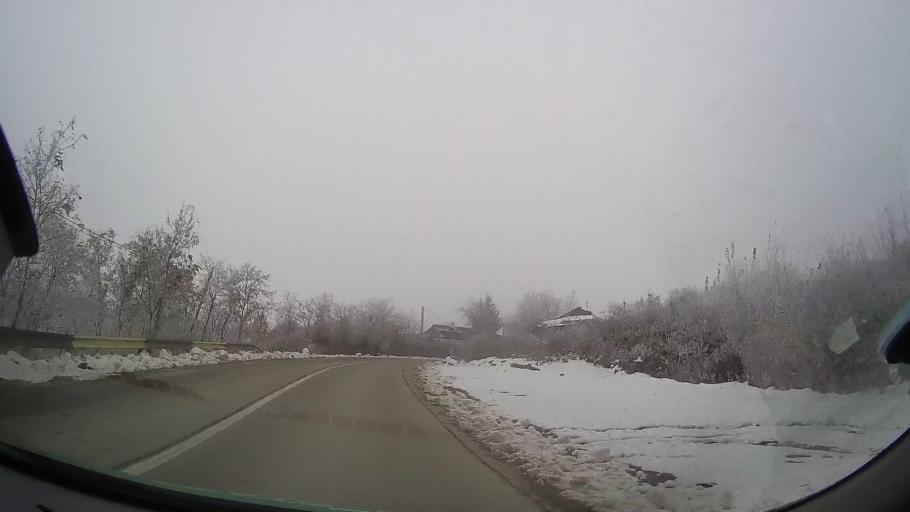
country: RO
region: Vaslui
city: Coroiesti
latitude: 46.2171
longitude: 27.4409
